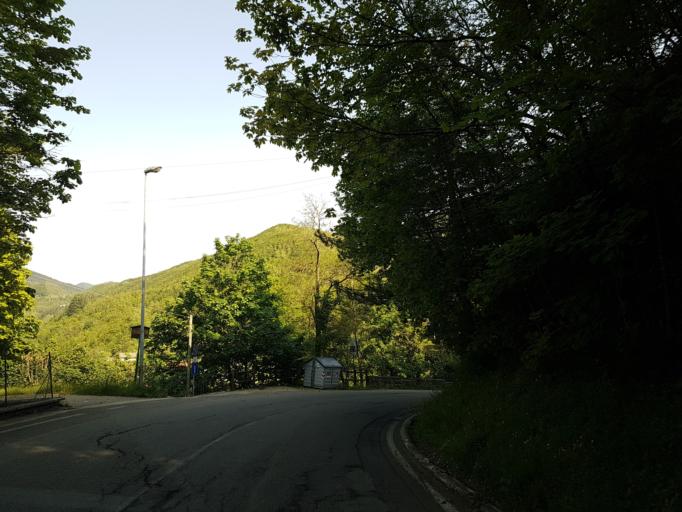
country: IT
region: Tuscany
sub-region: Province of Arezzo
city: Soci
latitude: 43.7916
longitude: 11.8773
